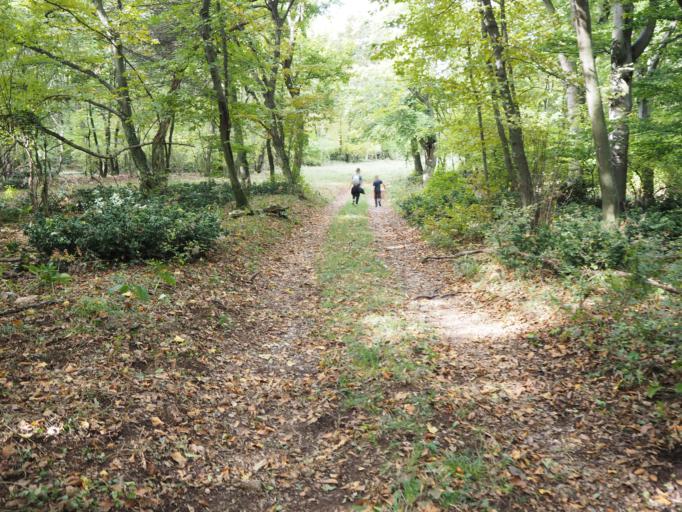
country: HU
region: Baranya
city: Pecs
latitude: 46.1119
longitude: 18.1747
